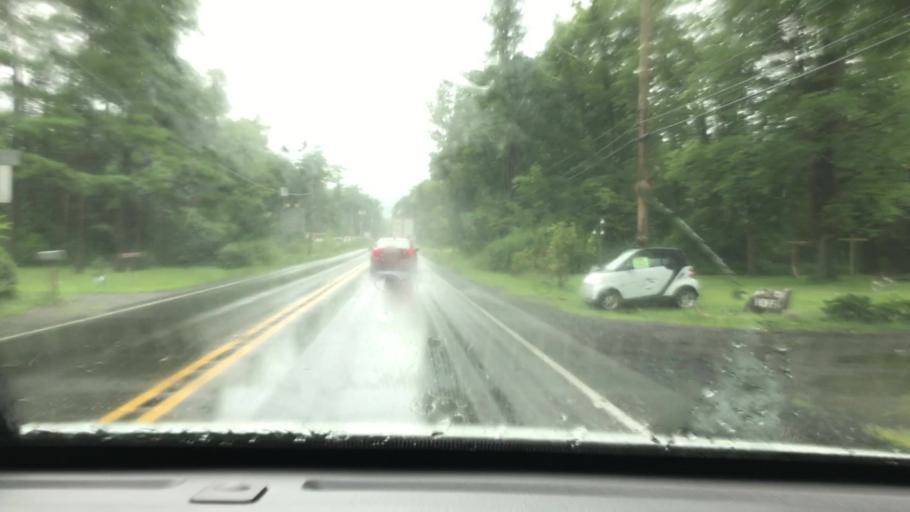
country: US
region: Pennsylvania
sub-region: Blair County
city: Tyrone
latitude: 40.7272
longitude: -78.1885
